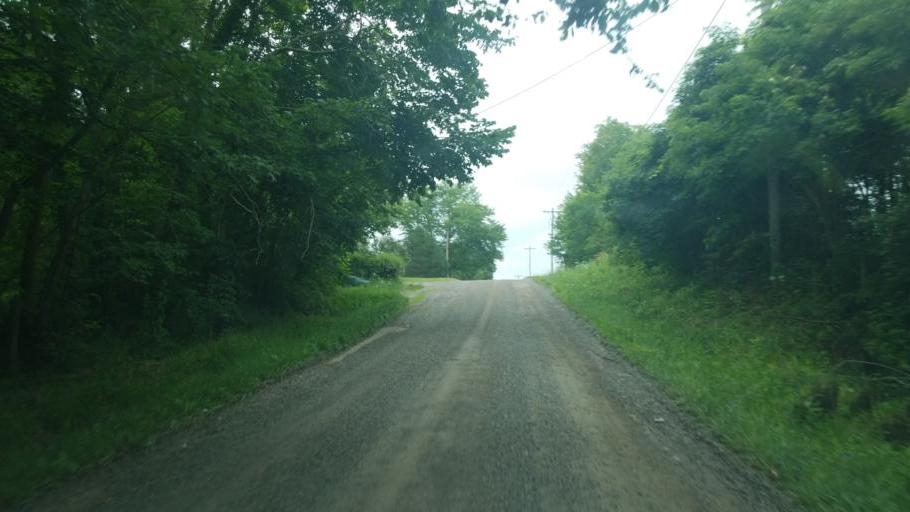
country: US
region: Ohio
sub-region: Morrow County
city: Mount Gilead
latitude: 40.4233
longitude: -82.7760
